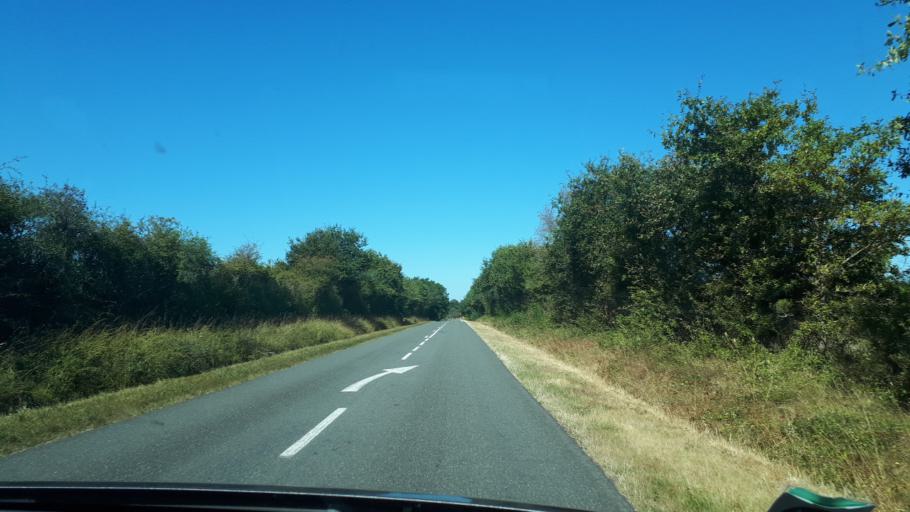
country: FR
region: Centre
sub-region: Departement du Loiret
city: Cerdon
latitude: 47.6397
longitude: 2.4090
